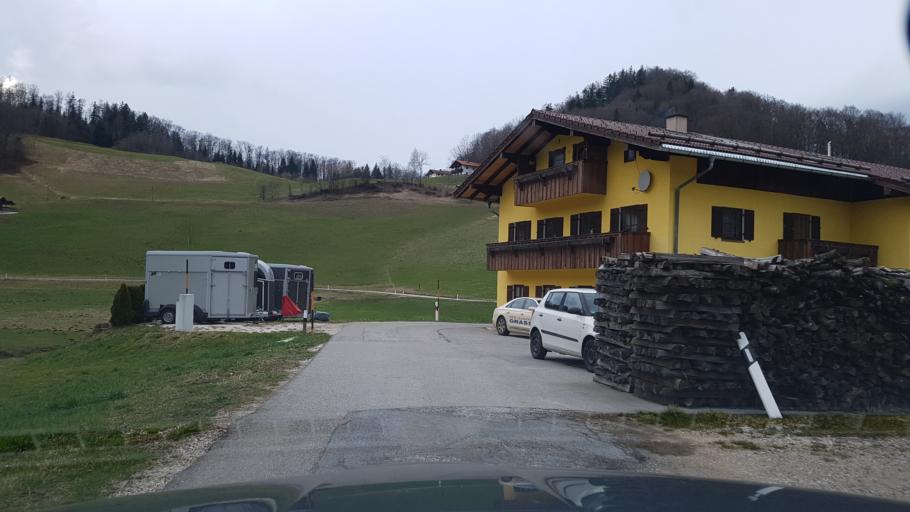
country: DE
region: Bavaria
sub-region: Upper Bavaria
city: Marktschellenberg
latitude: 47.6777
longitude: 13.0683
